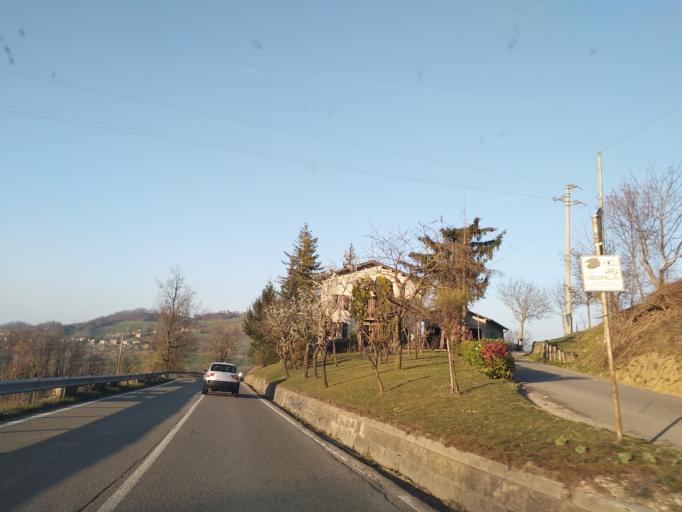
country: IT
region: Emilia-Romagna
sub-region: Provincia di Reggio Emilia
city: Castelnovo ne'Monti
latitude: 44.4340
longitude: 10.4220
